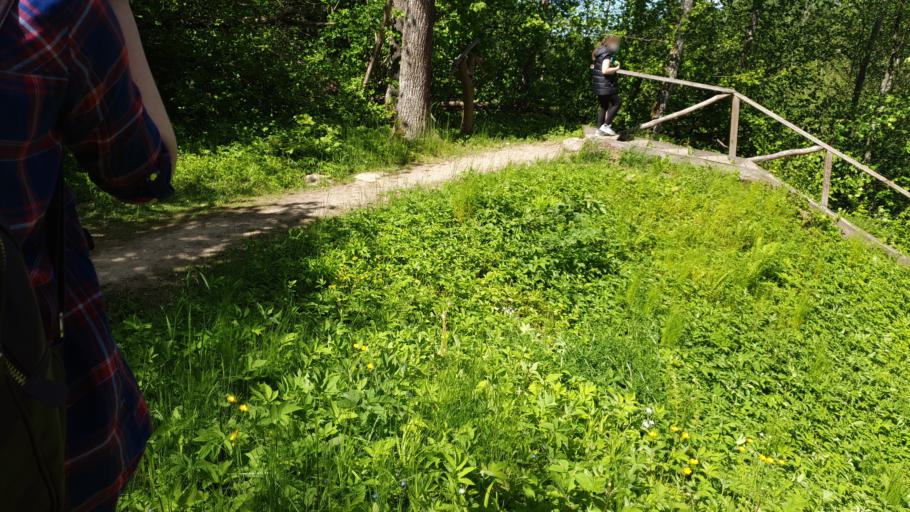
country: LT
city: Moletai
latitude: 55.0745
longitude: 25.4143
